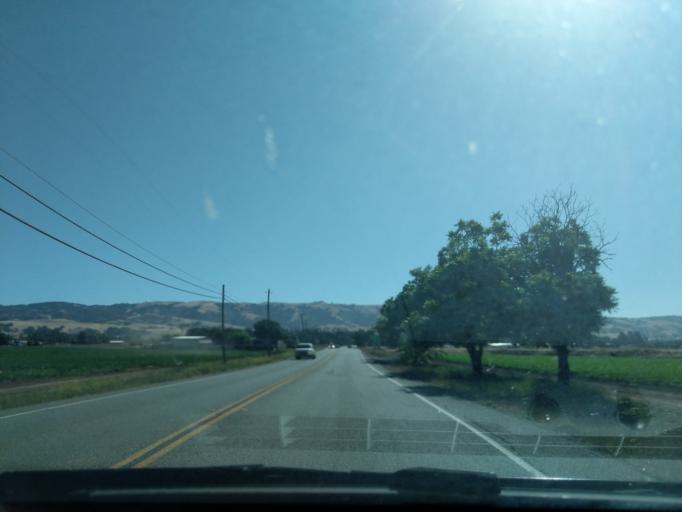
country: US
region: California
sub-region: Santa Clara County
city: Gilroy
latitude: 37.0327
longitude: -121.5399
